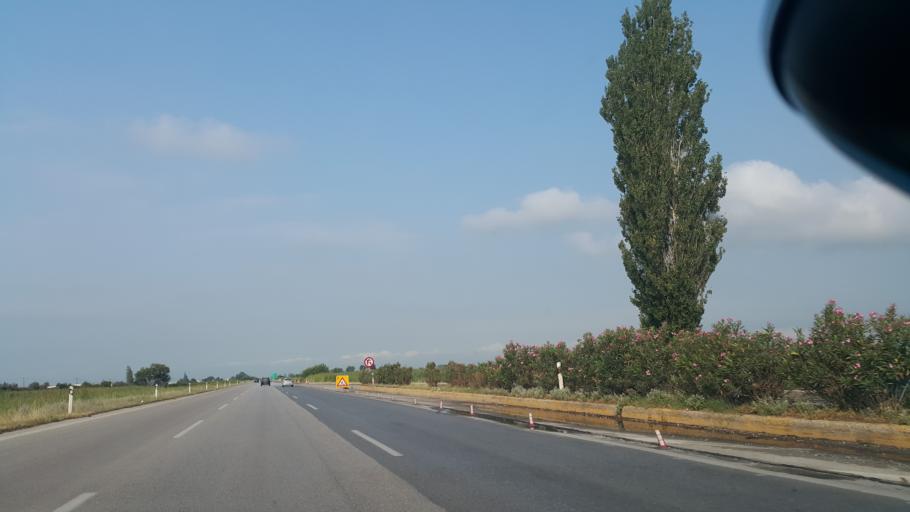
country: GR
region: Central Macedonia
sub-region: Nomos Thessalonikis
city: Chalastra
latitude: 40.6261
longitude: 22.7662
